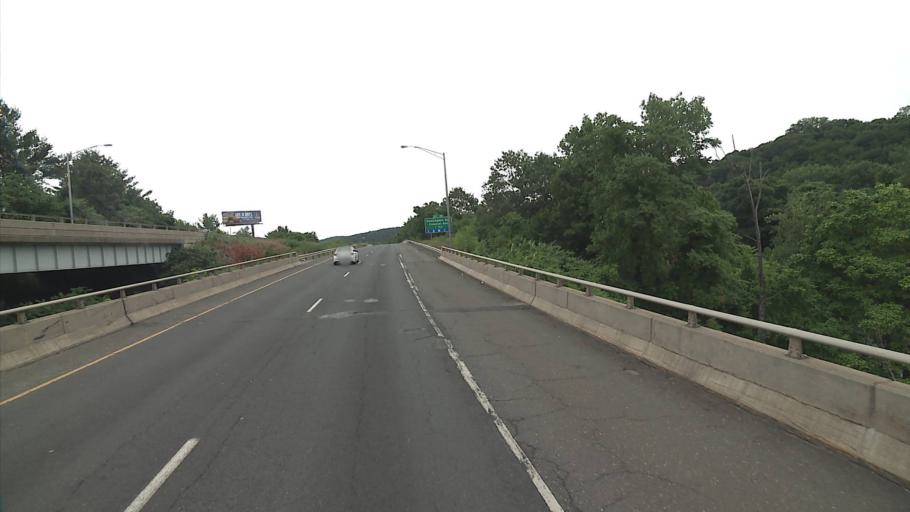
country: US
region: Connecticut
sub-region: New Haven County
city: Waterbury
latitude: 41.5683
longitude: -73.0570
